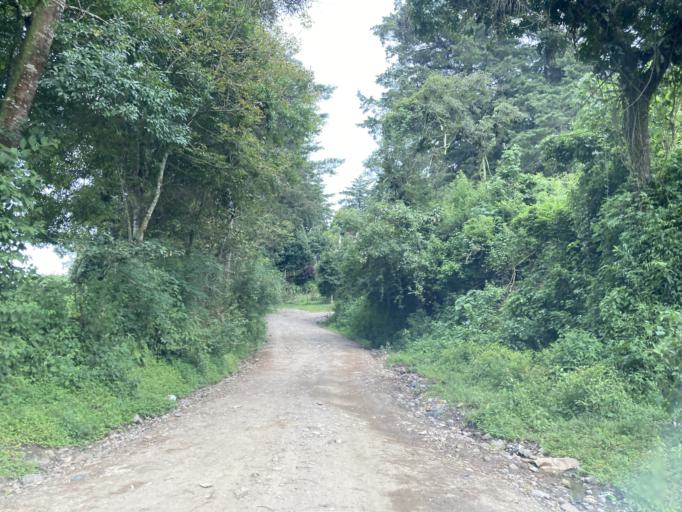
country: GT
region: Guatemala
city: San Jose Pinula
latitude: 14.5364
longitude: -90.4066
